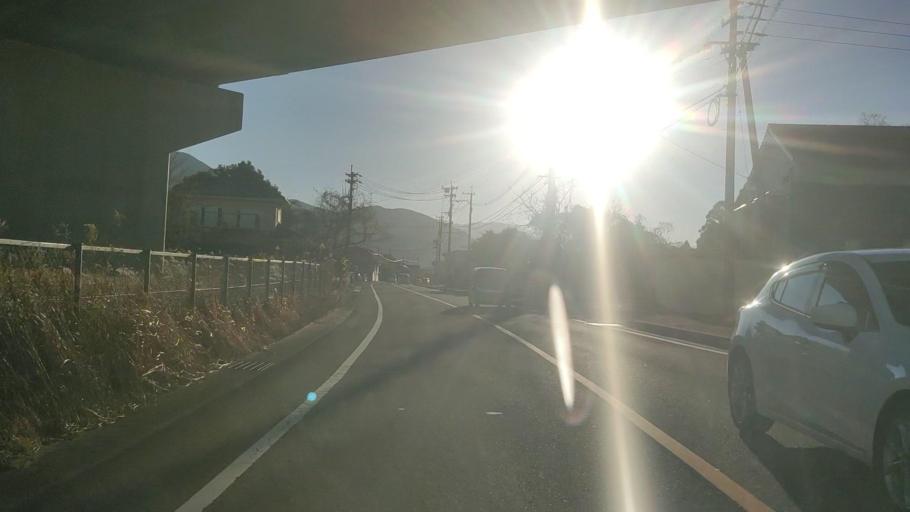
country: JP
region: Miyazaki
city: Miyazaki-shi
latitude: 31.8524
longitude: 131.3571
